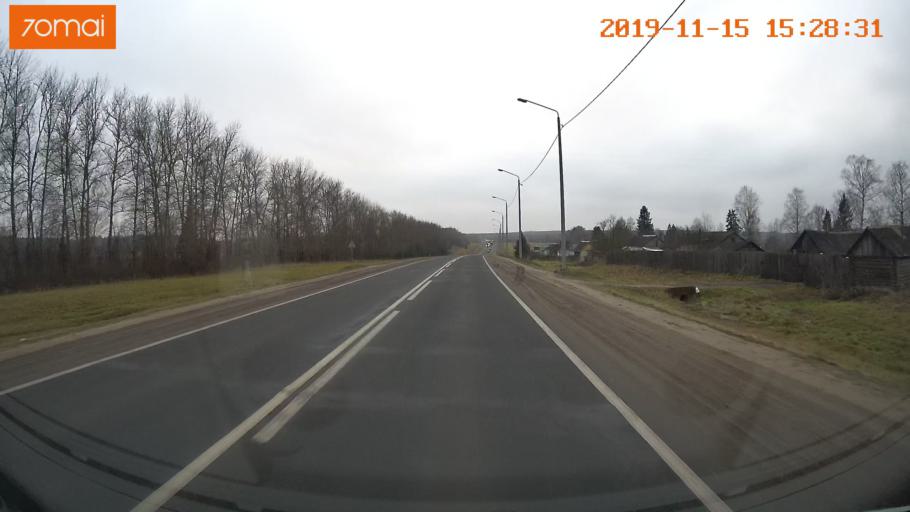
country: RU
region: Jaroslavl
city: Danilov
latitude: 58.1314
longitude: 40.1341
